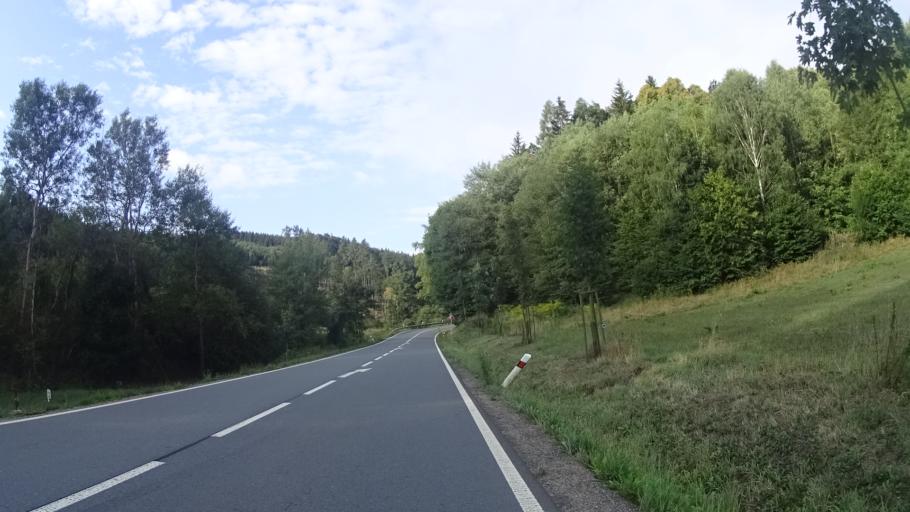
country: CZ
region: Olomoucky
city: Stity
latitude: 49.8654
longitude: 16.7261
